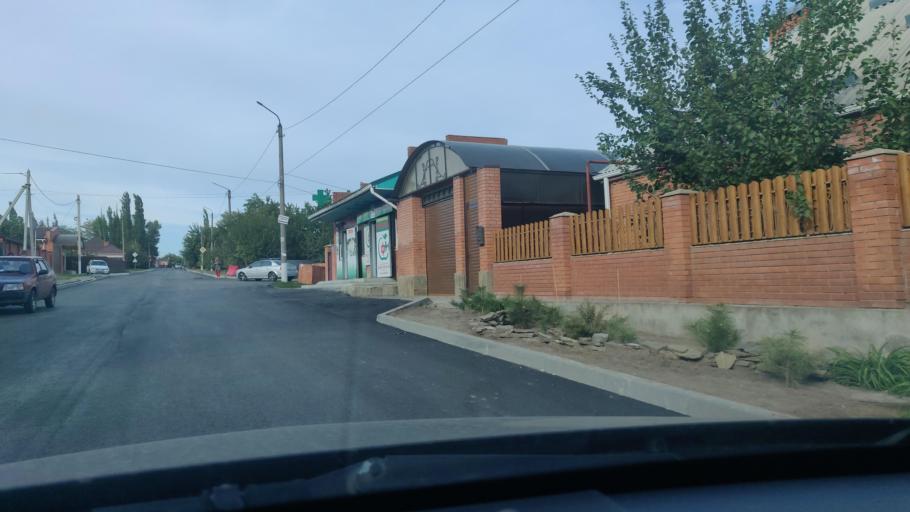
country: RU
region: Rostov
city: Ust'-Donetskiy
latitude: 47.6441
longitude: 40.8731
